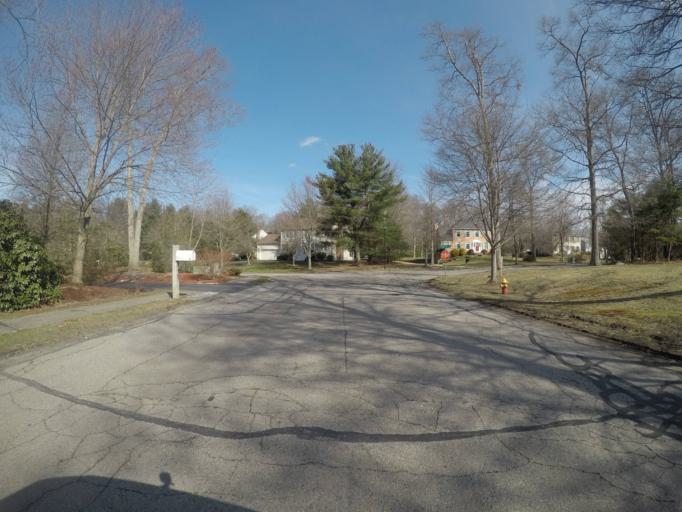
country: US
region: Massachusetts
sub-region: Bristol County
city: Easton
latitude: 42.0202
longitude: -71.1626
